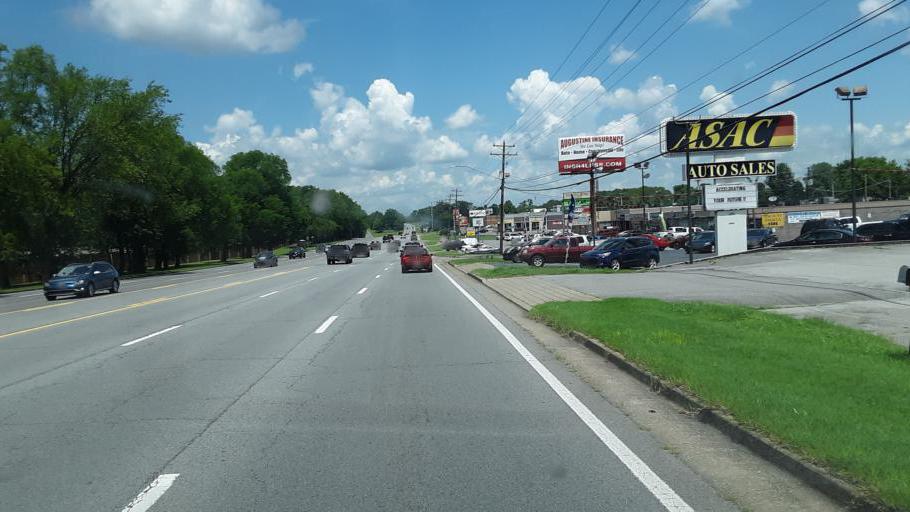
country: US
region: Kentucky
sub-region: Christian County
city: Fort Campbell North
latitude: 36.6255
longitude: -87.4328
